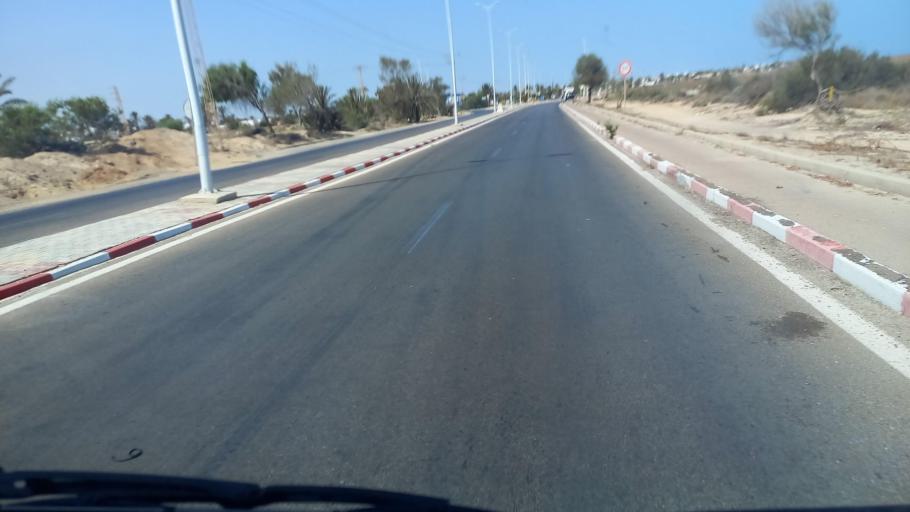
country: TN
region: Madanin
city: Midoun
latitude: 33.8690
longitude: 10.9474
